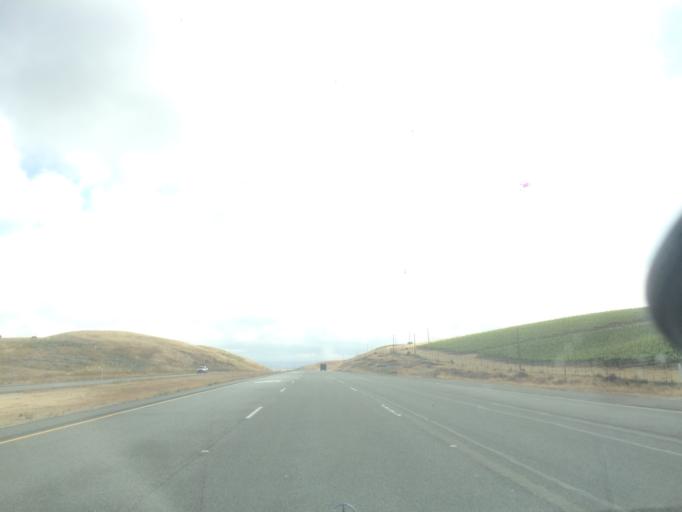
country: US
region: California
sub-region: San Luis Obispo County
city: Shandon
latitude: 35.6548
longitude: -120.5279
